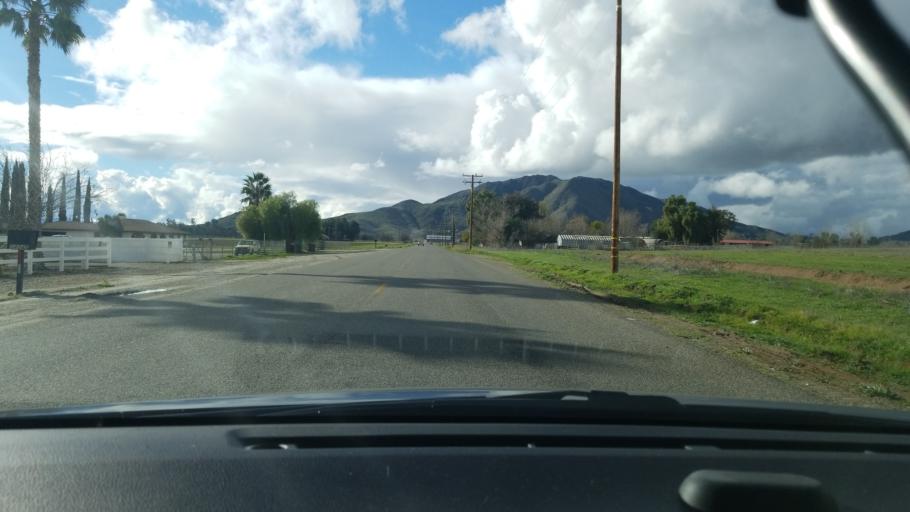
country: US
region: California
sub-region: Riverside County
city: Green Acres
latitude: 33.7220
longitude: -117.0617
